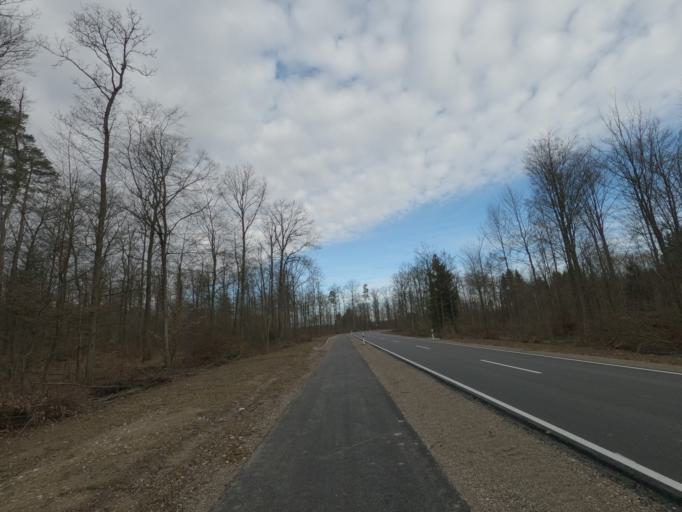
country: DE
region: Baden-Wuerttemberg
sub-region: Regierungsbezirk Stuttgart
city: Ohmden
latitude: 48.6587
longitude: 9.5274
